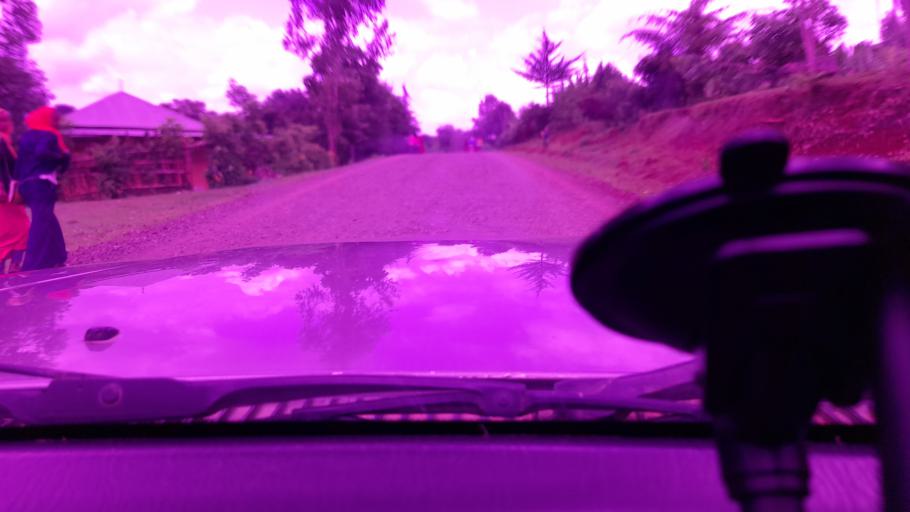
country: ET
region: Oromiya
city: Jima
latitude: 7.9891
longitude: 37.4832
